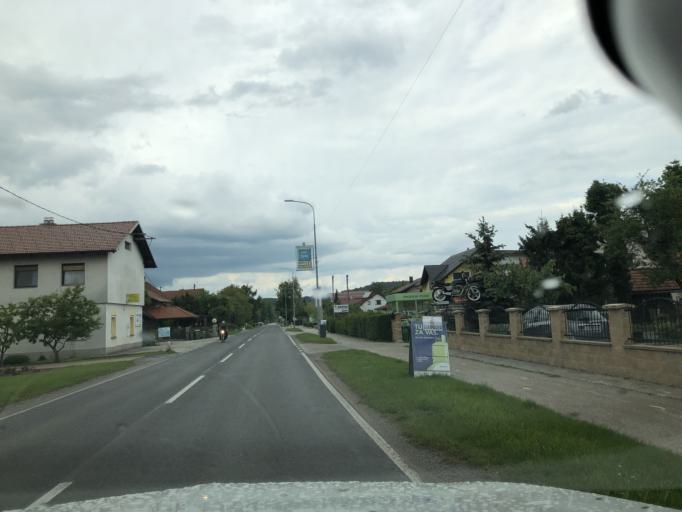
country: SI
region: Cerknica
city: Cerknica
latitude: 45.7942
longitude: 14.3598
